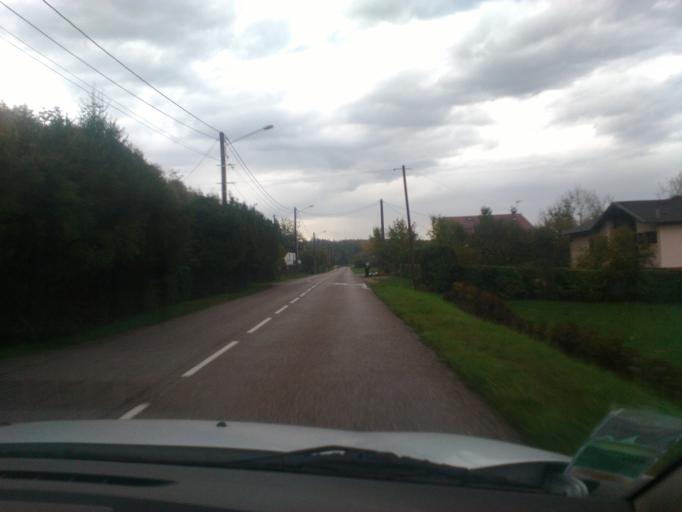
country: FR
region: Lorraine
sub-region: Departement des Vosges
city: Chatel-sur-Moselle
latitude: 48.3022
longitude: 6.4118
